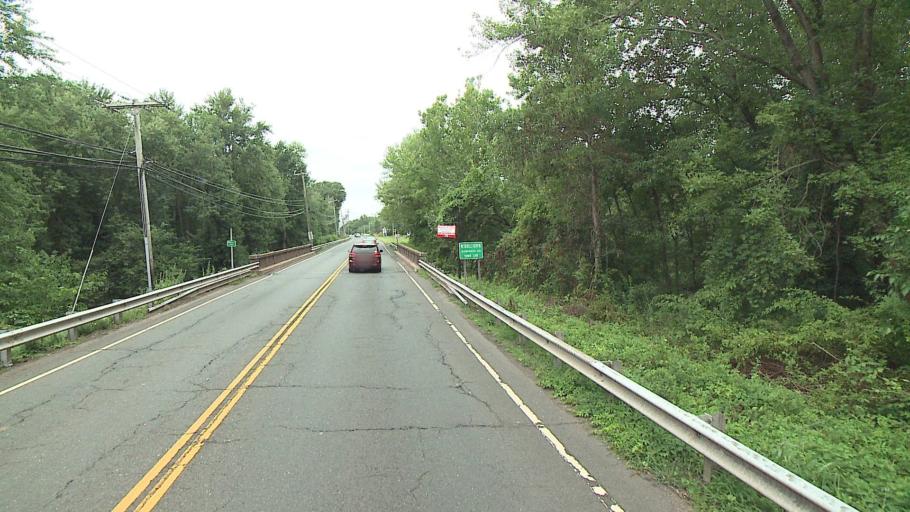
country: US
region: Connecticut
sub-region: Middlesex County
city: Cromwell
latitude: 41.5982
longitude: -72.6771
